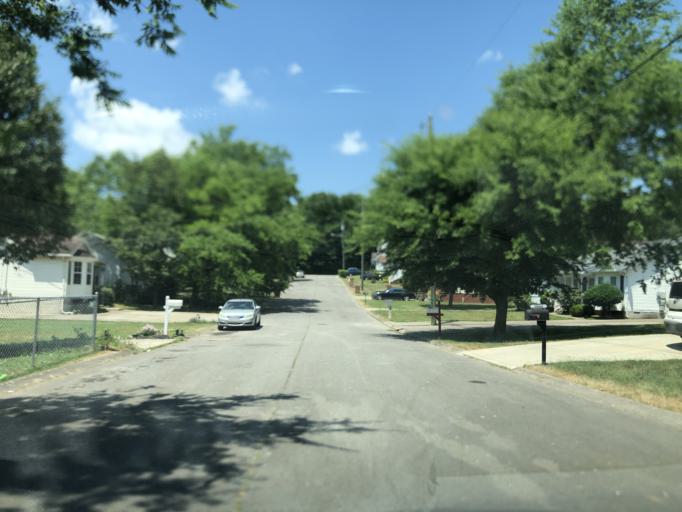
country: US
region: Tennessee
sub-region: Davidson County
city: Goodlettsville
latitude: 36.2703
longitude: -86.7176
